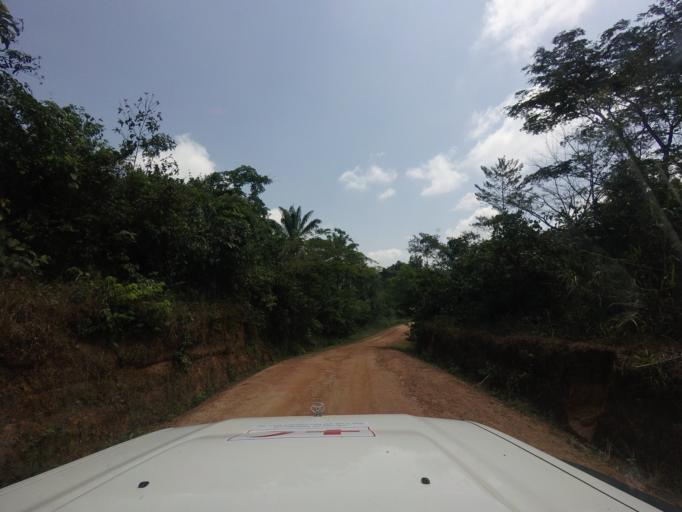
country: LR
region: Lofa
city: Voinjama
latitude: 8.4899
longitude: -9.6550
